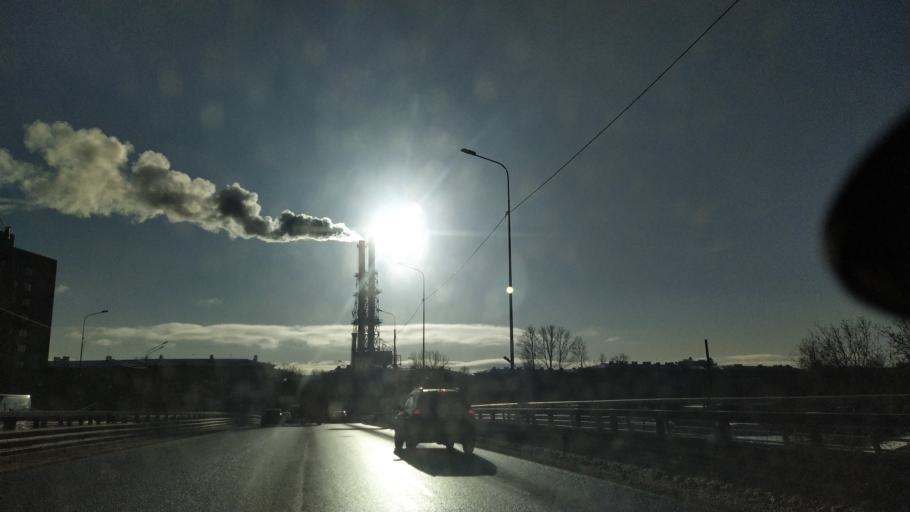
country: RU
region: Leningrad
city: Chernaya Rechka
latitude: 59.9921
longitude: 30.2987
